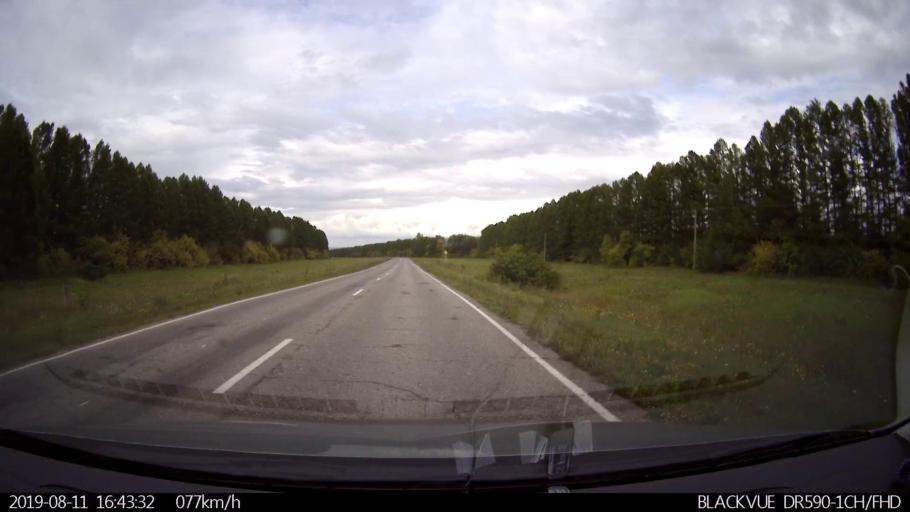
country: RU
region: Ulyanovsk
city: Mayna
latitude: 54.1701
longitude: 47.6733
